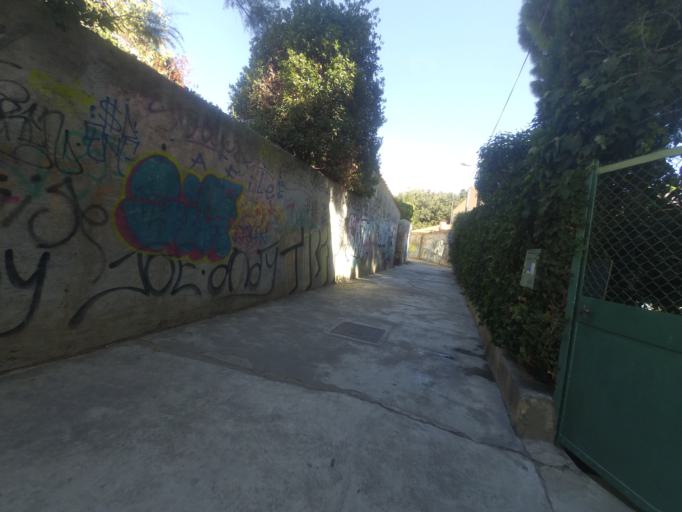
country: FR
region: Languedoc-Roussillon
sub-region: Departement des Pyrenees-Orientales
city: Perpignan
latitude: 42.6982
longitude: 2.8838
